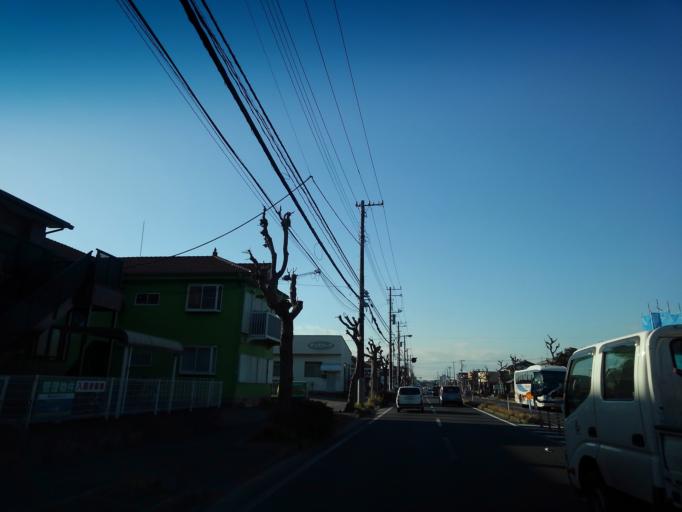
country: JP
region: Chiba
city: Kimitsu
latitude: 35.3294
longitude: 139.8969
